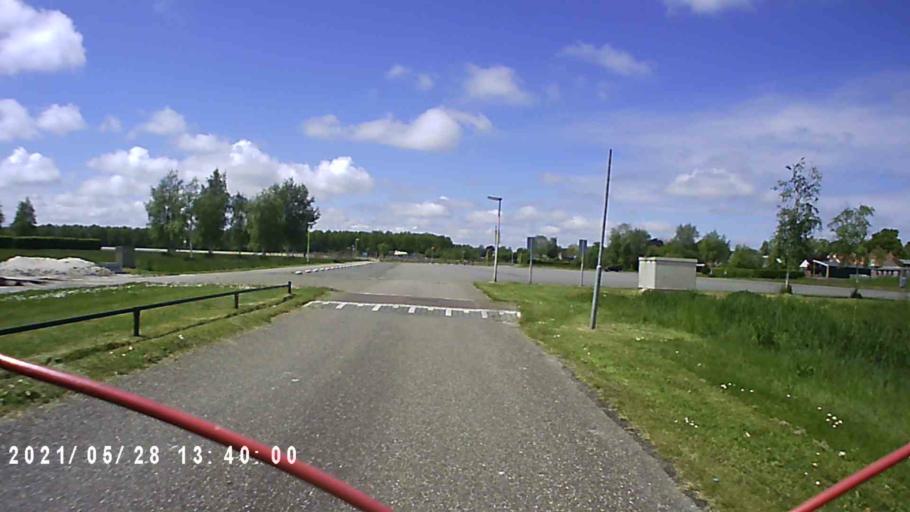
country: NL
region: Groningen
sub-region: Gemeente  Oldambt
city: Winschoten
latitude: 53.1965
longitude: 7.0294
